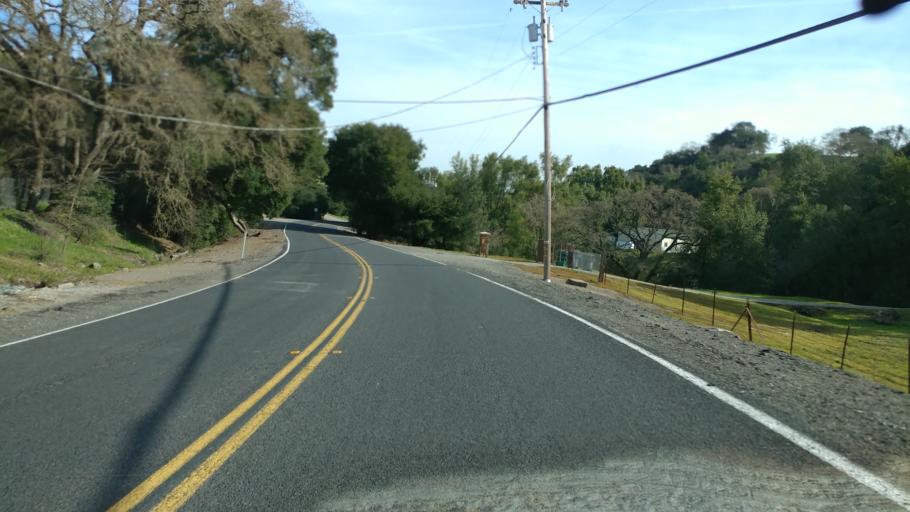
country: US
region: California
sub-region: Contra Costa County
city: Danville
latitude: 37.8074
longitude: -122.0381
